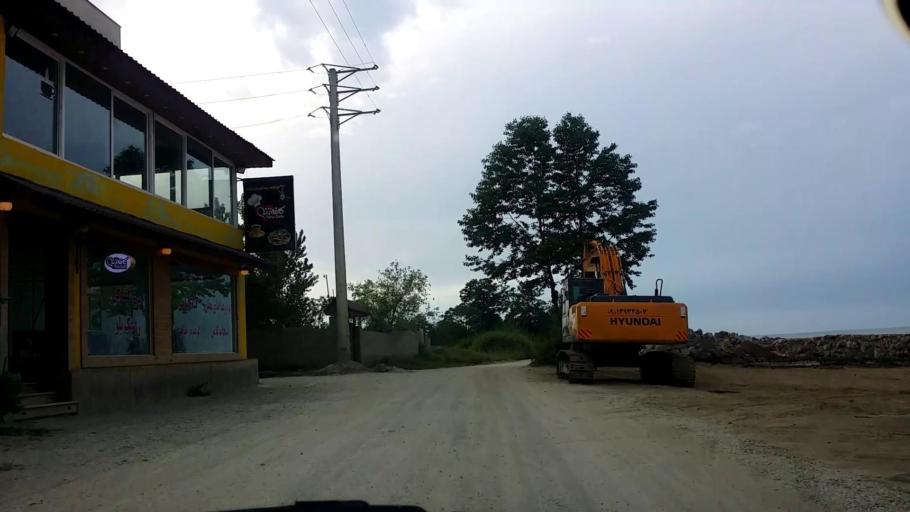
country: IR
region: Mazandaran
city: Chalus
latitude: 36.6840
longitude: 51.4304
